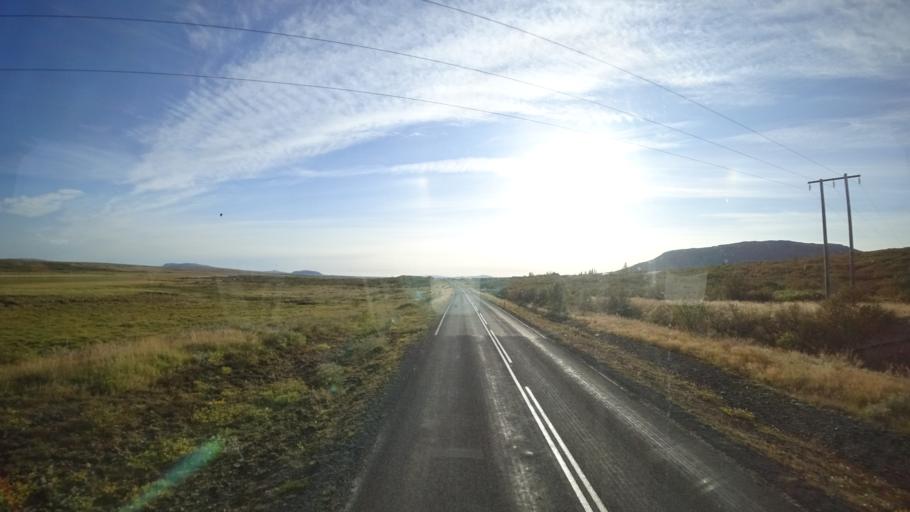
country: IS
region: South
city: Selfoss
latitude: 64.2561
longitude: -20.4808
